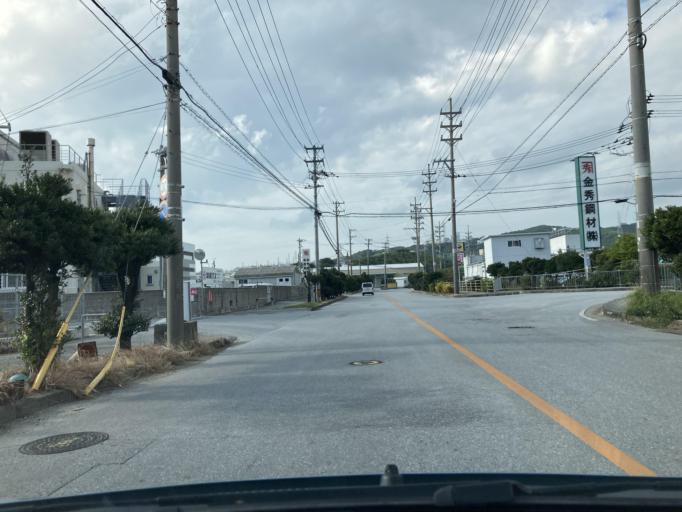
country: JP
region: Okinawa
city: Ginowan
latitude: 26.2279
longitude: 127.7761
